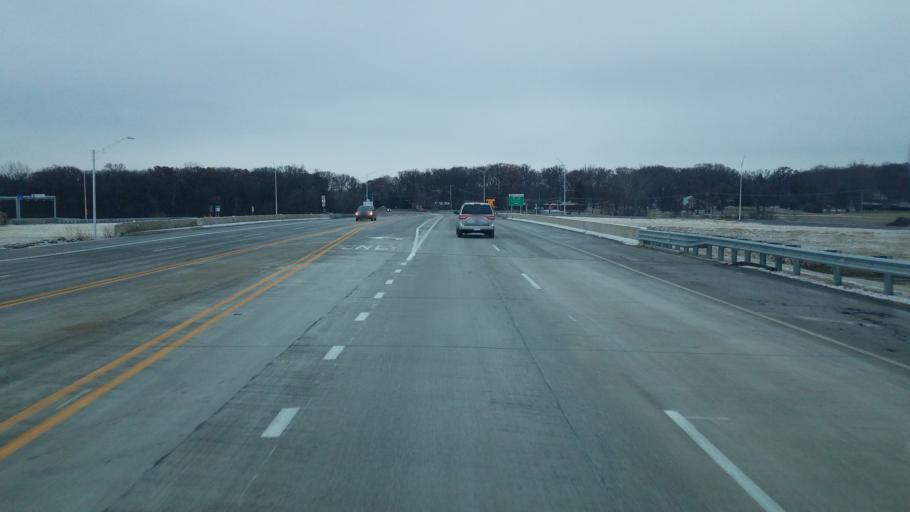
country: US
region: Illinois
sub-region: Kane County
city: Sugar Grove
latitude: 41.8192
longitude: -88.4667
